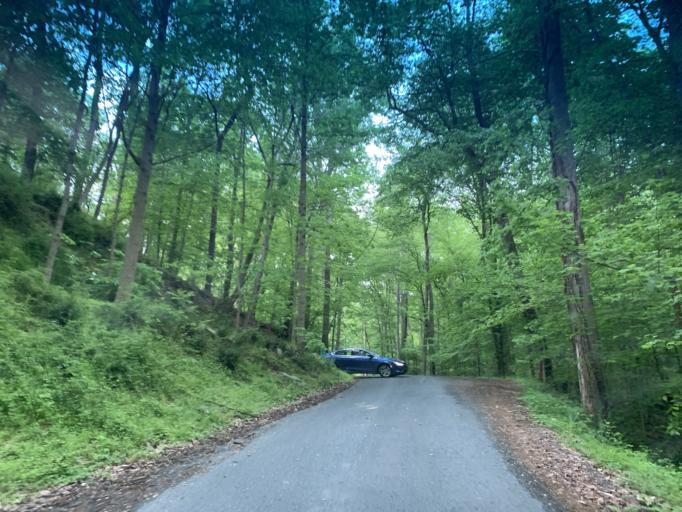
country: US
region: Pennsylvania
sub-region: York County
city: Susquehanna Trails
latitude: 39.7035
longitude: -76.2615
